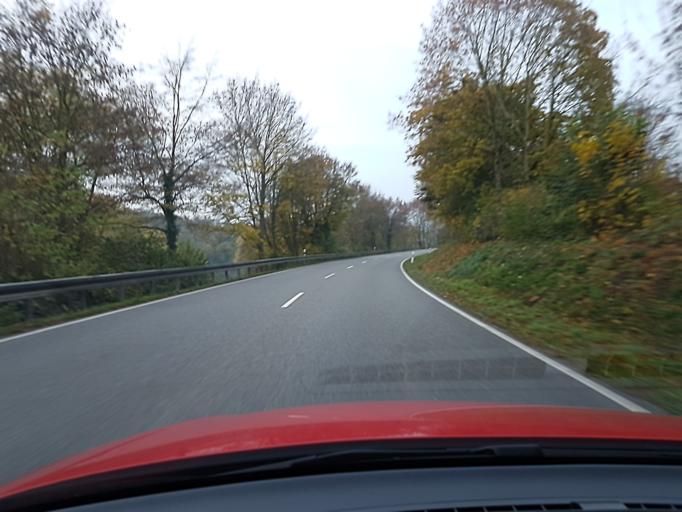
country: DE
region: Baden-Wuerttemberg
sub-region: Regierungsbezirk Stuttgart
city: Walheim
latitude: 49.0112
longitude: 9.1580
